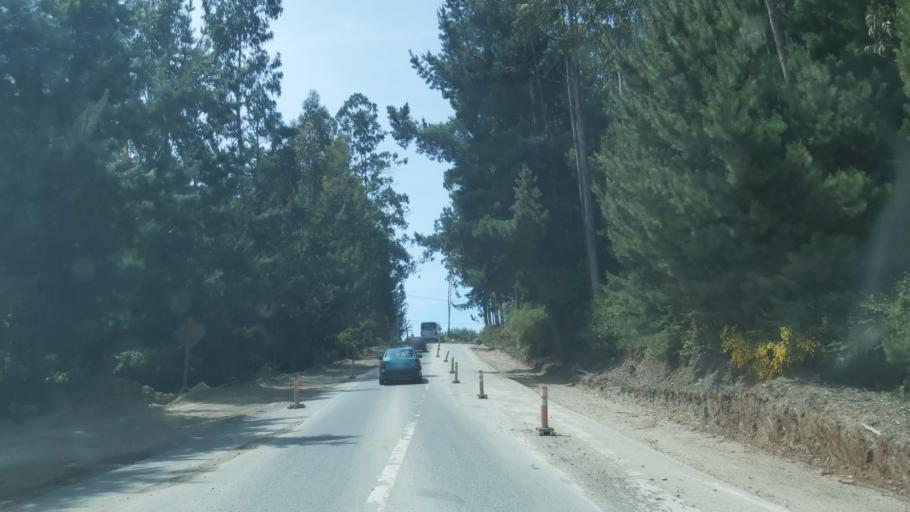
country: CL
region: Maule
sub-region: Provincia de Talca
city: Constitucion
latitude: -35.3773
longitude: -72.4218
